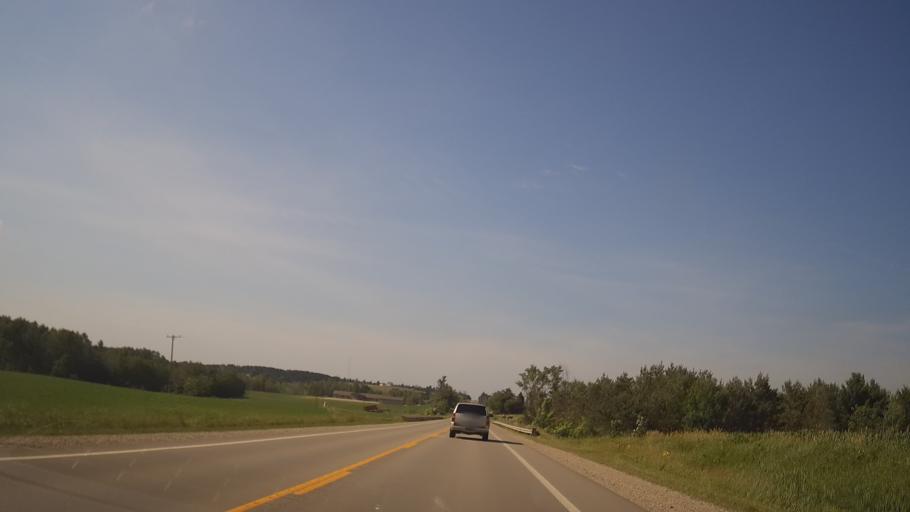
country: US
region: Michigan
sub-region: Ogemaw County
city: West Branch
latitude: 44.2848
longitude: -84.1257
